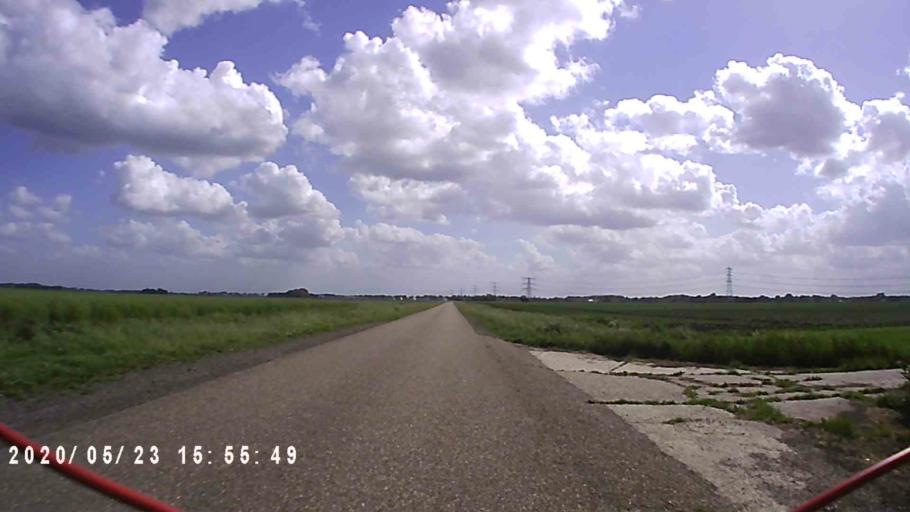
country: NL
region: Groningen
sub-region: Gemeente Delfzijl
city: Delfzijl
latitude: 53.2624
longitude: 6.9006
